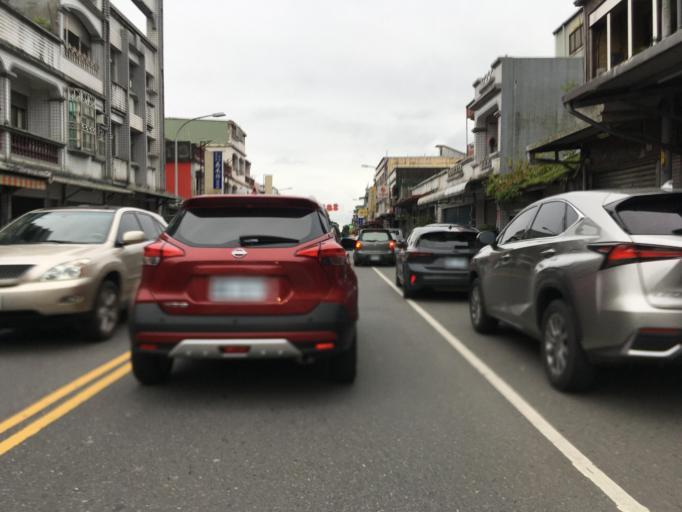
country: TW
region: Taiwan
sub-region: Yilan
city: Yilan
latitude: 24.6618
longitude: 121.6219
